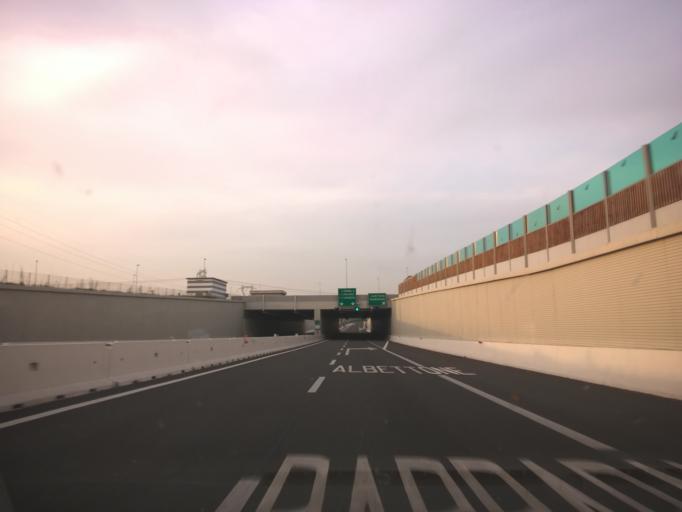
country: IT
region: Veneto
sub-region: Provincia di Vicenza
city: Albettone
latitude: 45.3788
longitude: 11.6114
